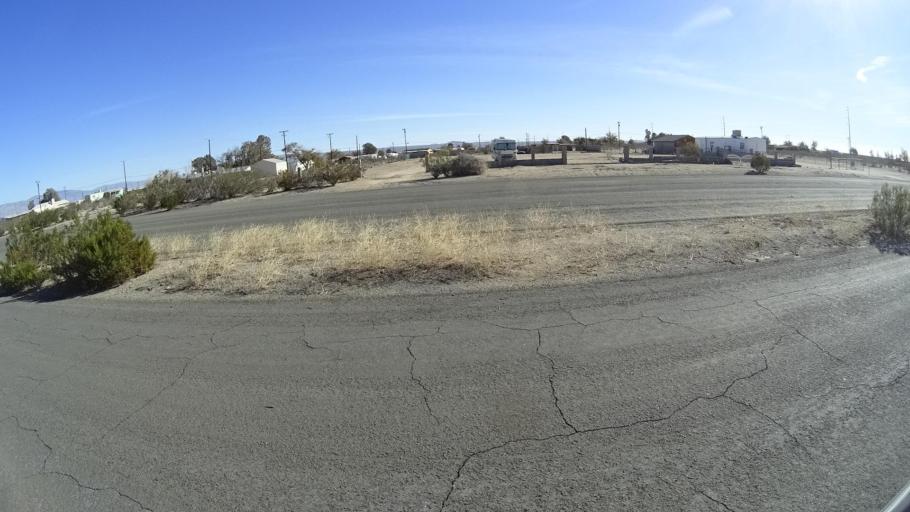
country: US
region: California
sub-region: Kern County
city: California City
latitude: 35.2011
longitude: -118.0215
